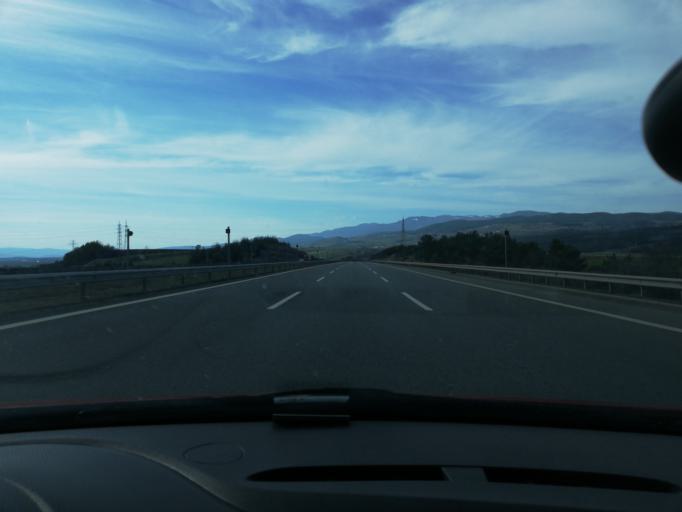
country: TR
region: Bolu
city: Bolu
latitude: 40.7682
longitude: 31.7434
